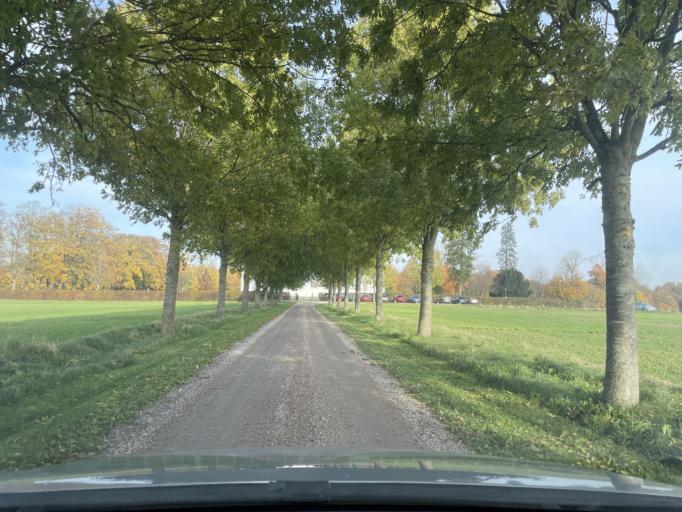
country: SE
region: Skane
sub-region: Eslovs Kommun
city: Eslov
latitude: 55.8628
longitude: 13.2435
